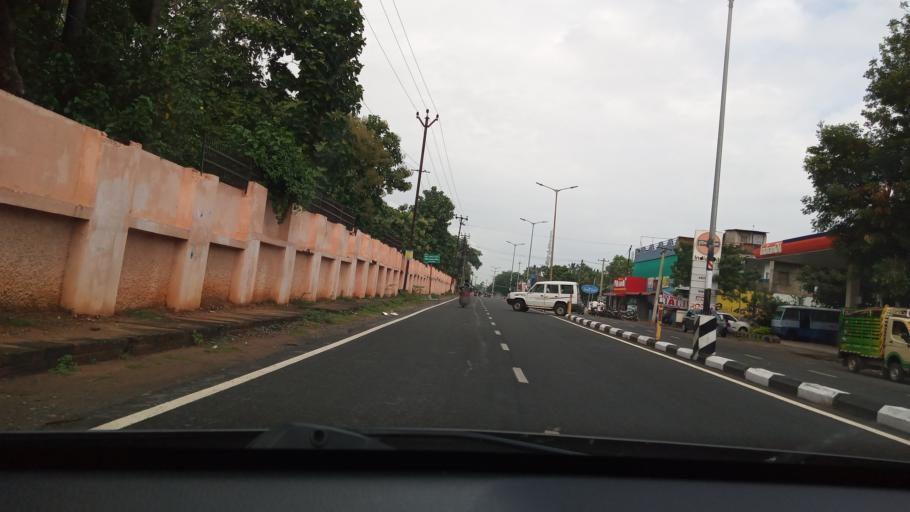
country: IN
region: Tamil Nadu
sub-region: Villupuram
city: Auroville
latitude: 12.0138
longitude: 79.8579
